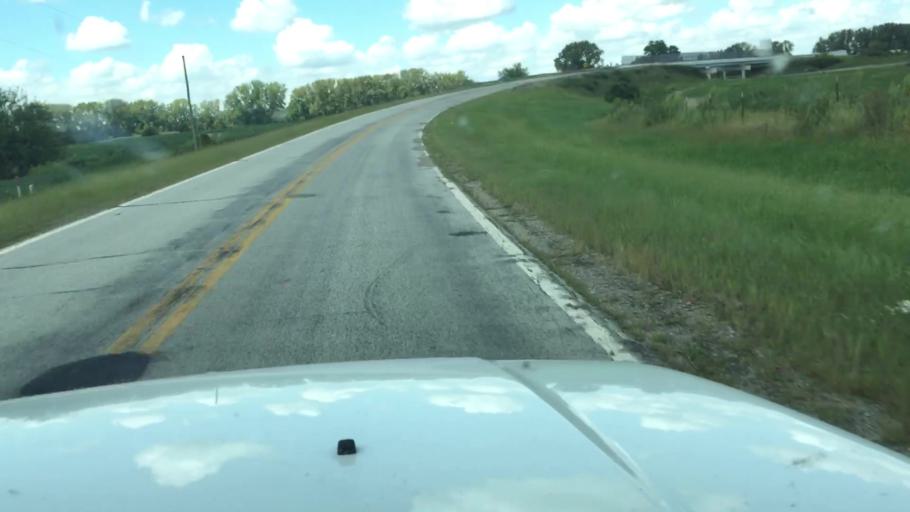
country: US
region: Ohio
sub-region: Madison County
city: Choctaw Lake
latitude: 39.9354
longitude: -83.5688
